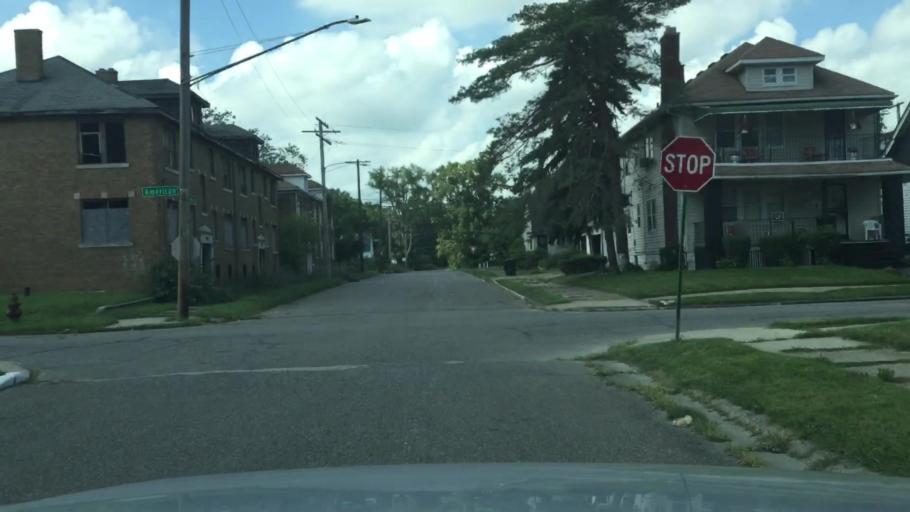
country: US
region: Michigan
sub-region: Wayne County
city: Dearborn
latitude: 42.3570
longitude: -83.1440
